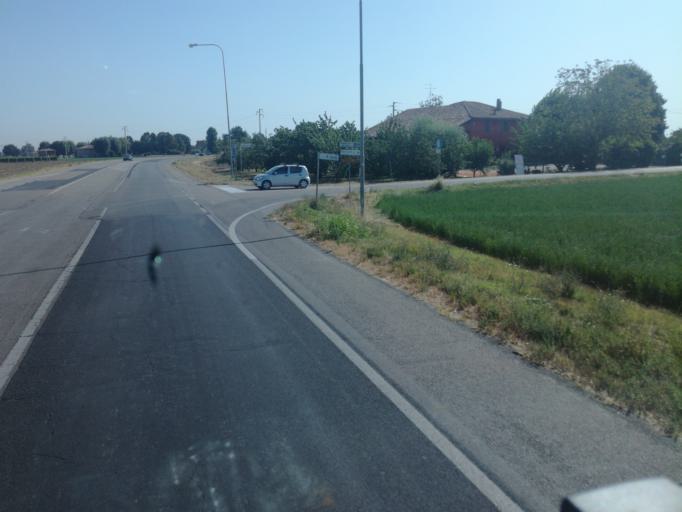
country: IT
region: Emilia-Romagna
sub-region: Provincia di Bologna
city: Castel San Pietro Terme
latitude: 44.4142
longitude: 11.5942
